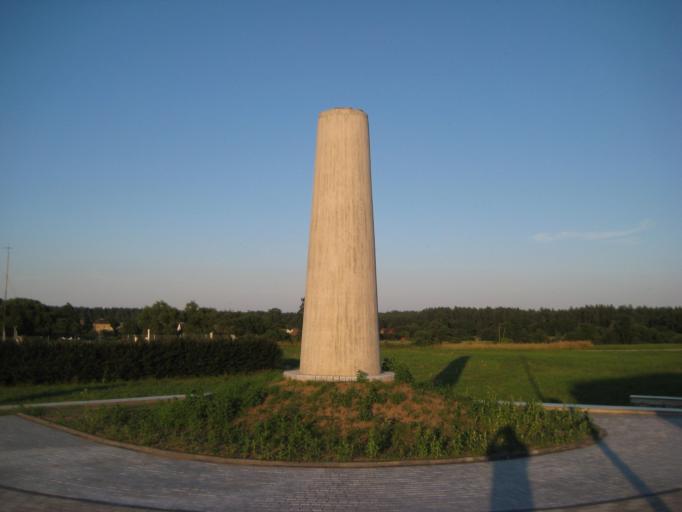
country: LT
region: Alytaus apskritis
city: Varena
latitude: 54.2485
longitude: 24.5507
